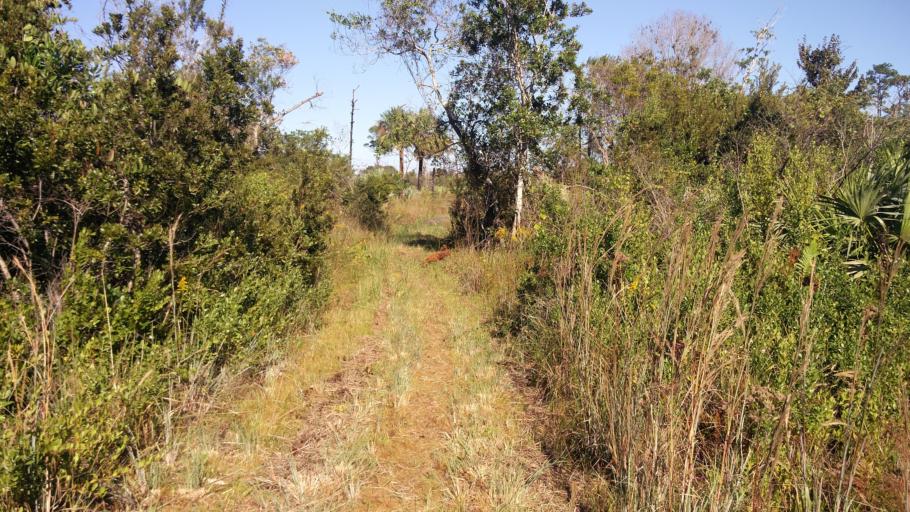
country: US
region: Florida
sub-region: Palm Beach County
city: Tequesta
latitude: 27.0071
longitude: -80.1194
